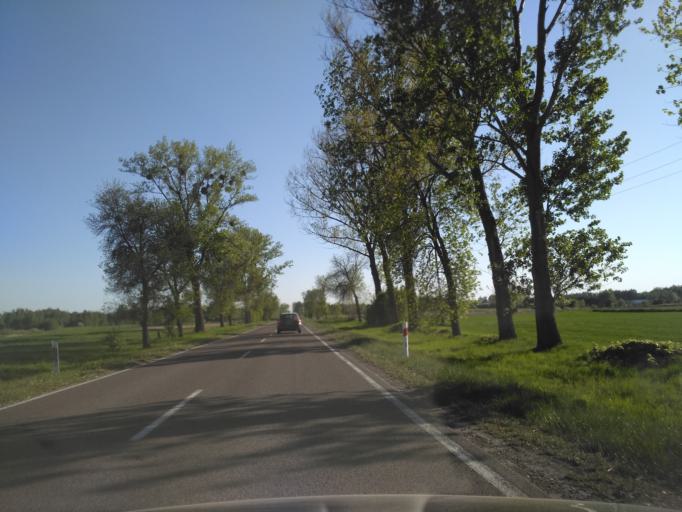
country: PL
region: Lublin Voivodeship
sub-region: Powiat leczynski
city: Cycow
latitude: 51.2179
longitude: 23.0753
